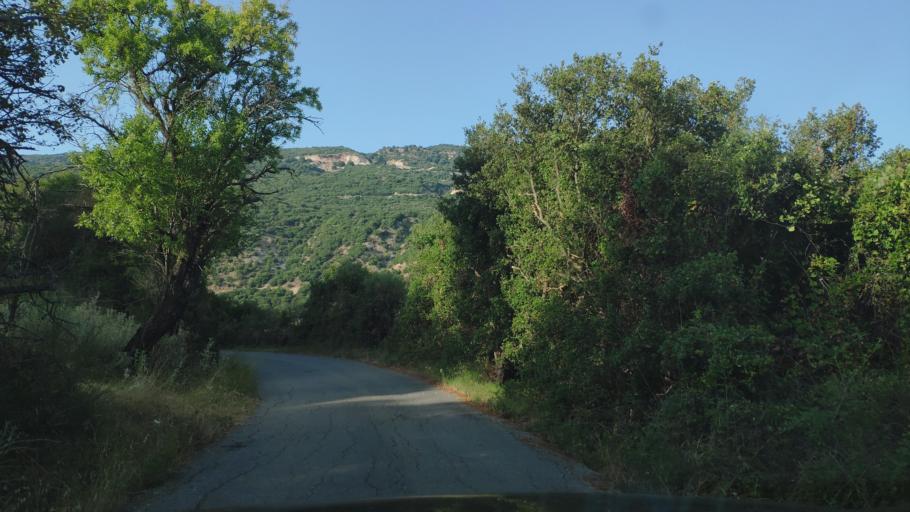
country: GR
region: West Greece
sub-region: Nomos Aitolias kai Akarnanias
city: Monastirakion
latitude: 38.8504
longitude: 20.9794
